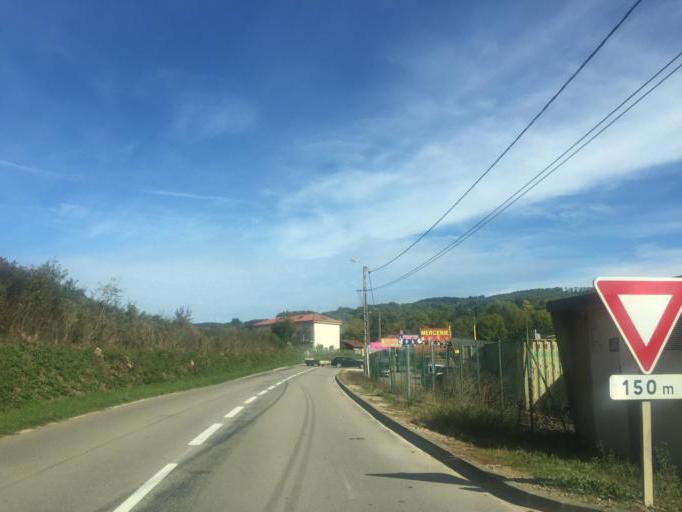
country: FR
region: Franche-Comte
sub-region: Departement du Jura
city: Saint-Amour
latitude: 46.4450
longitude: 5.3404
